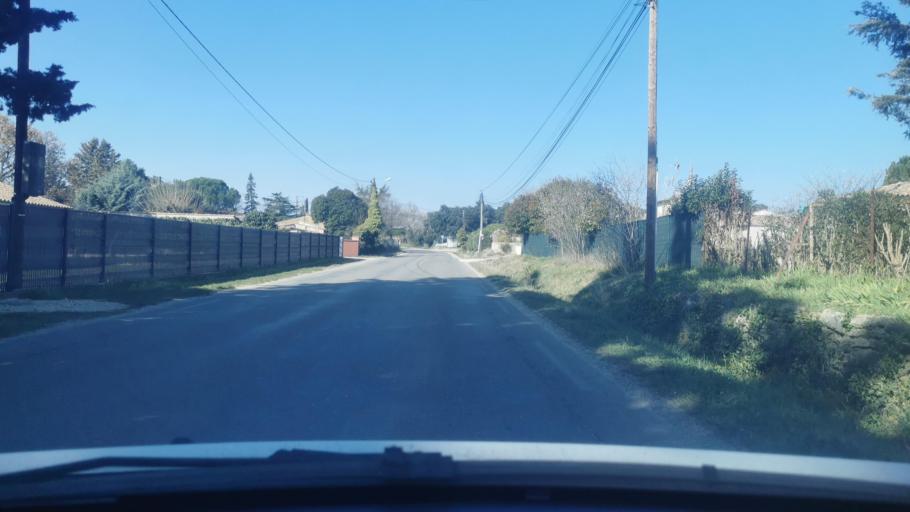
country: FR
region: Languedoc-Roussillon
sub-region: Departement du Gard
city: Saint-Quentin-la-Poterie
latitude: 44.0491
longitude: 4.4264
